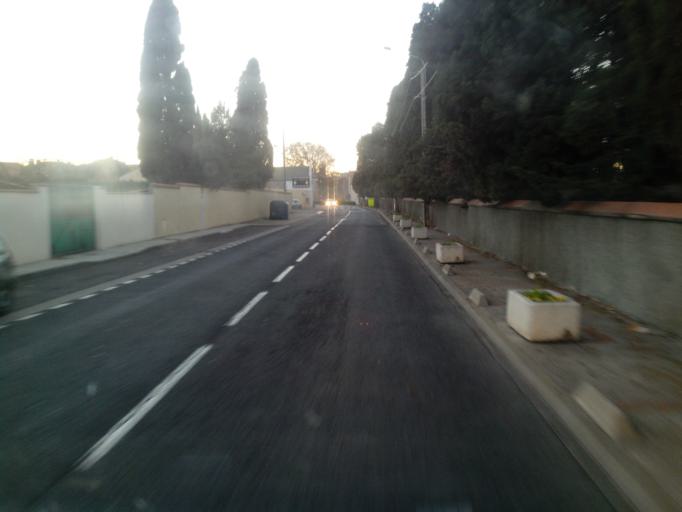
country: FR
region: Languedoc-Roussillon
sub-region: Departement des Pyrenees-Orientales
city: Rivesaltes
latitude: 42.7712
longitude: 2.8798
